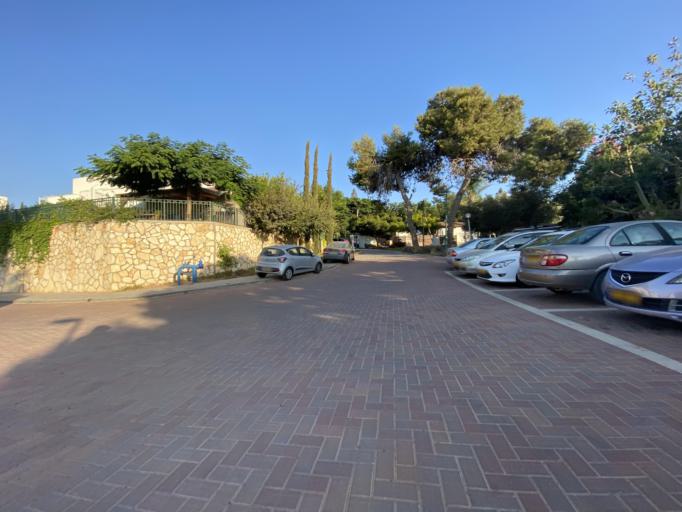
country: IL
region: Tel Aviv
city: Herzliyya
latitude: 32.1590
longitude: 34.8302
